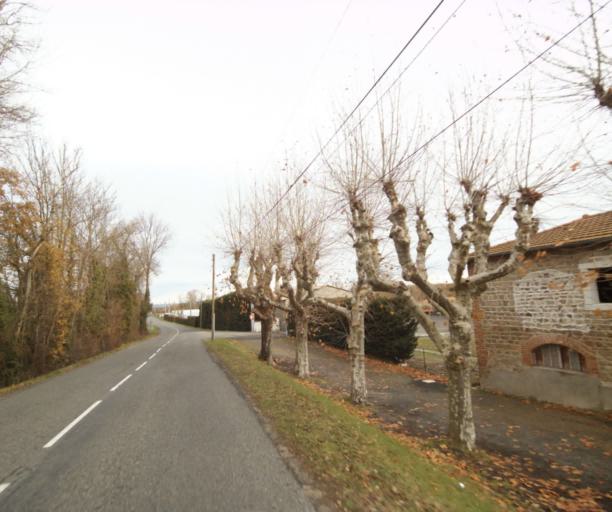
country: FR
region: Rhone-Alpes
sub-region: Departement de la Loire
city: Saint-Marcellin-en-Forez
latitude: 45.5130
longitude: 4.1787
